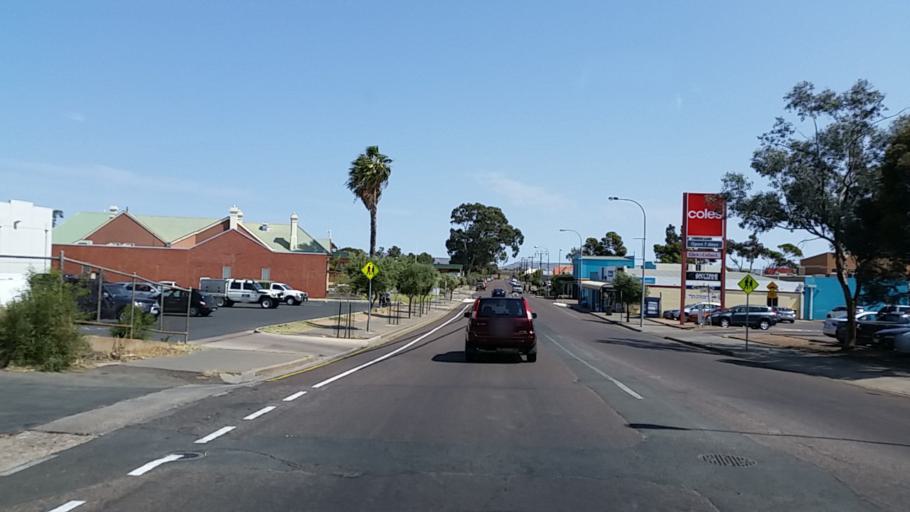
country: AU
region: South Australia
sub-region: Port Augusta
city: Port Augusta
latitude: -32.4930
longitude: 137.7651
